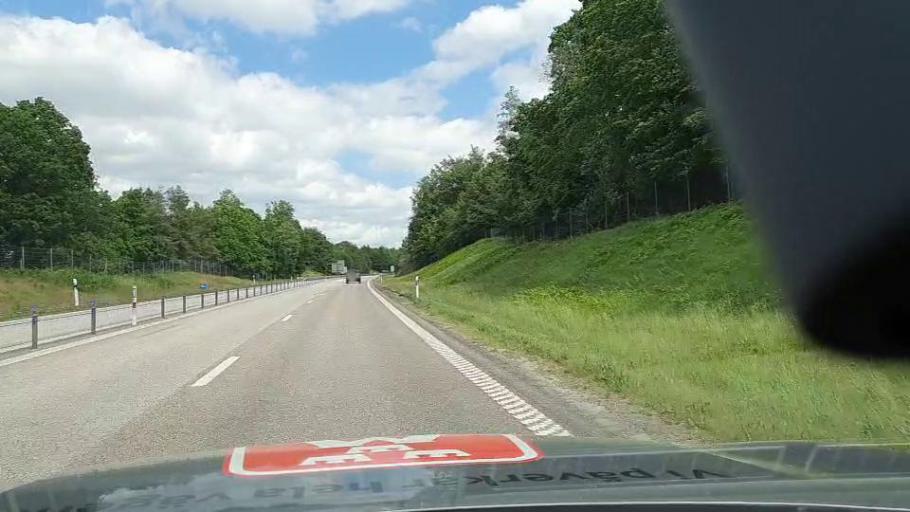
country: SE
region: Blekinge
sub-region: Ronneby Kommun
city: Brakne-Hoby
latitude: 56.2202
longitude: 15.1274
